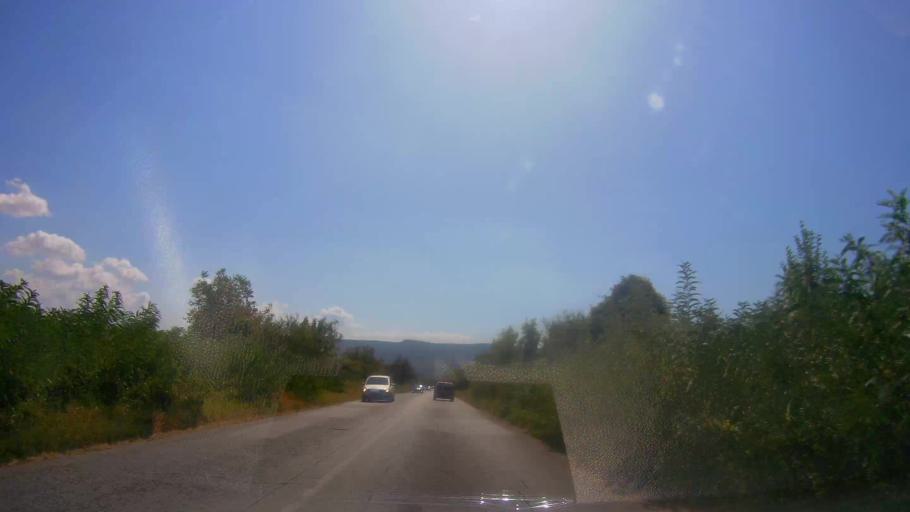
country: BG
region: Veliko Turnovo
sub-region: Obshtina Gorna Oryakhovitsa
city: Purvomaytsi
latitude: 43.1650
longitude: 25.6176
